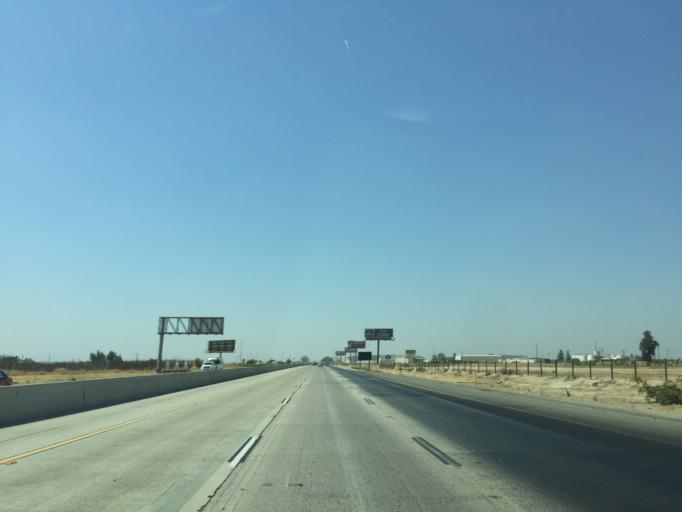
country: US
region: California
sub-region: Fresno County
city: Kingsburg
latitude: 36.5347
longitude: -119.5815
